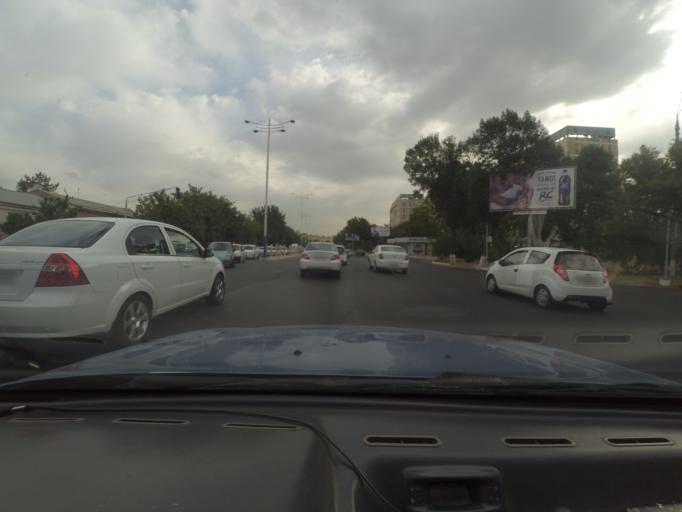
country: UZ
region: Toshkent
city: Salor
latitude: 41.3557
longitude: 69.3772
